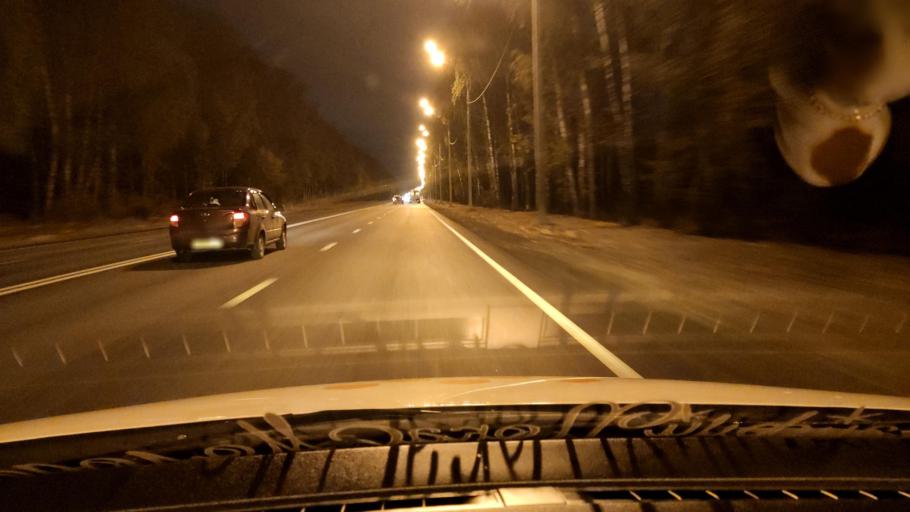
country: RU
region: Voronezj
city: Pridonskoy
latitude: 51.6943
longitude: 39.0917
